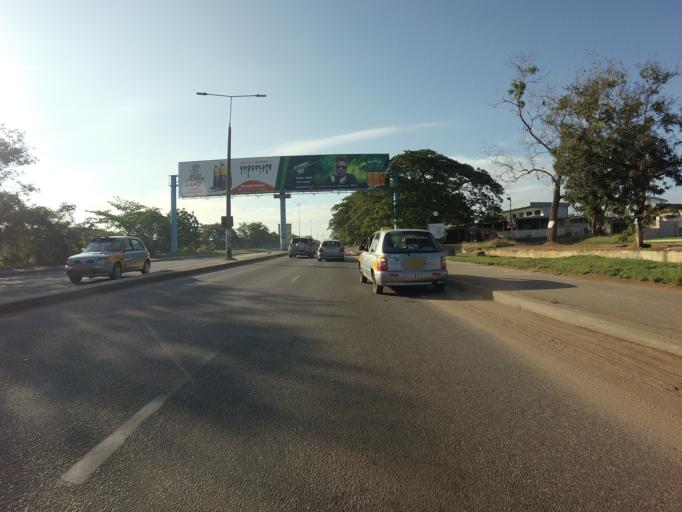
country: GH
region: Greater Accra
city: Accra
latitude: 5.5488
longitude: -0.2291
